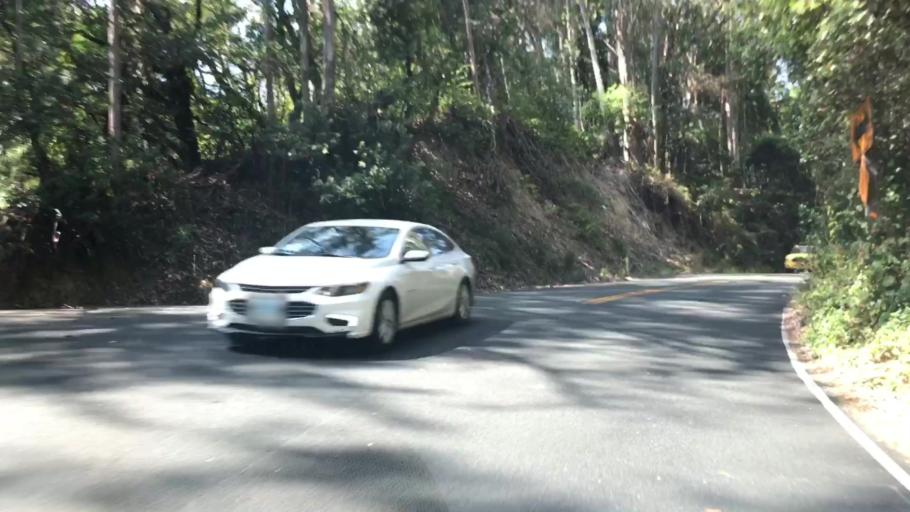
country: US
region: California
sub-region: Marin County
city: Bolinas
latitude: 37.9394
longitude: -122.7051
